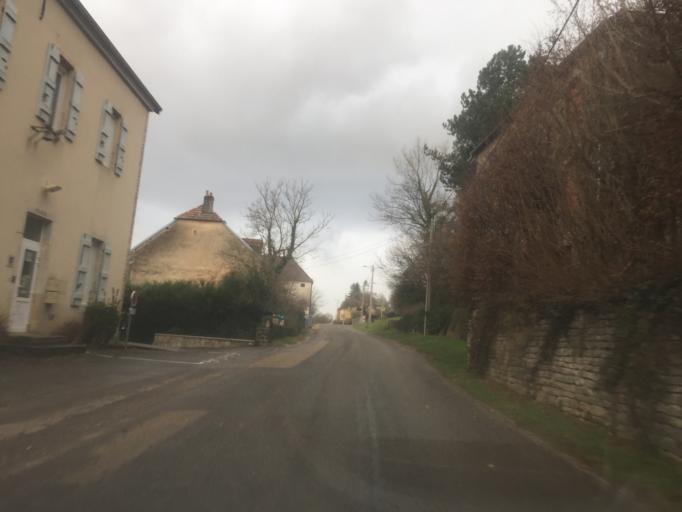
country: FR
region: Franche-Comte
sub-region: Departement du Jura
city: Orchamps
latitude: 47.2242
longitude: 5.6809
